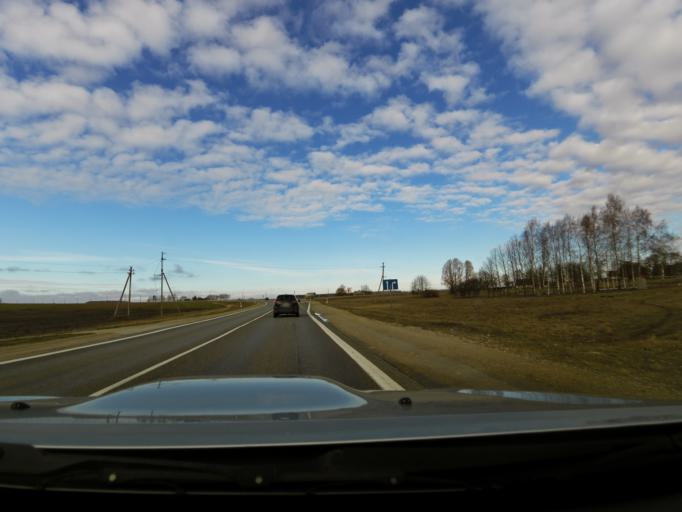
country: LT
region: Siauliu apskritis
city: Pakruojis
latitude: 55.7992
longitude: 24.0098
